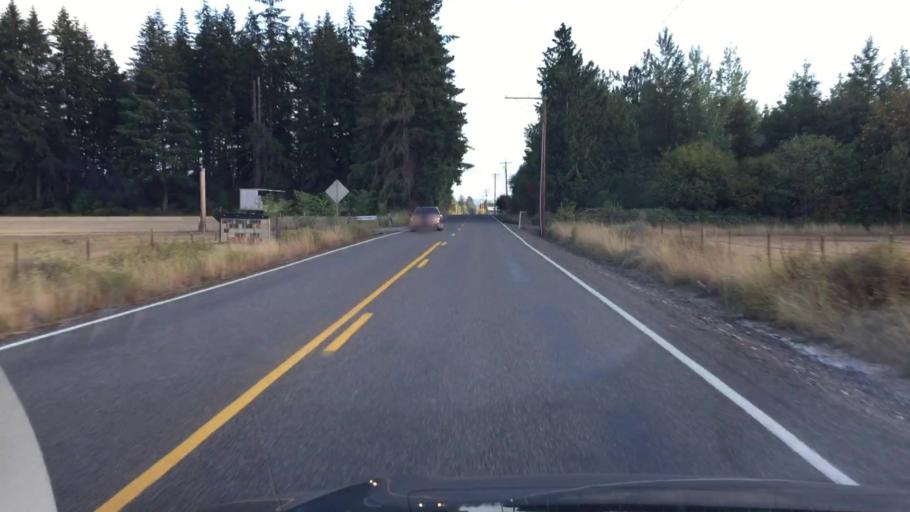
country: US
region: Washington
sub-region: Lewis County
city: Napavine
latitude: 46.5300
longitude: -122.7405
